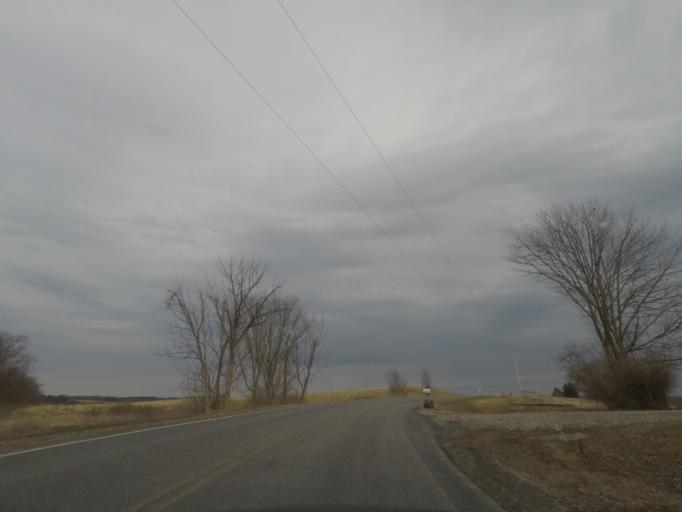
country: US
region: New York
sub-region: Washington County
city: Cambridge
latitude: 42.9676
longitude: -73.4674
